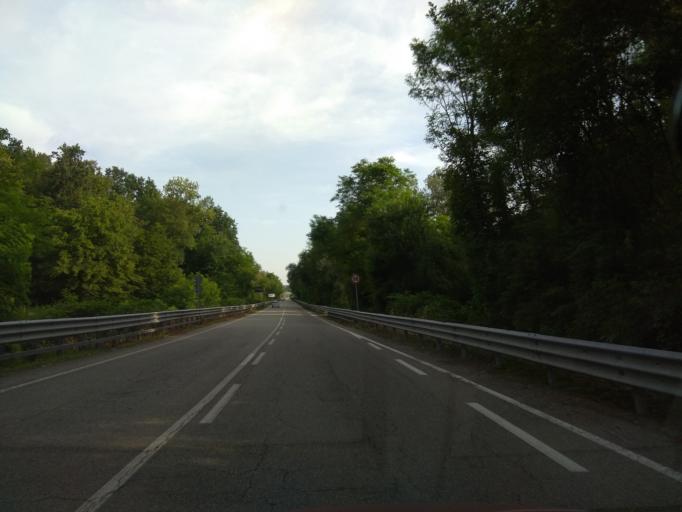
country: IT
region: Piedmont
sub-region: Provincia di Biella
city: Quaregna
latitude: 45.5746
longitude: 8.1688
